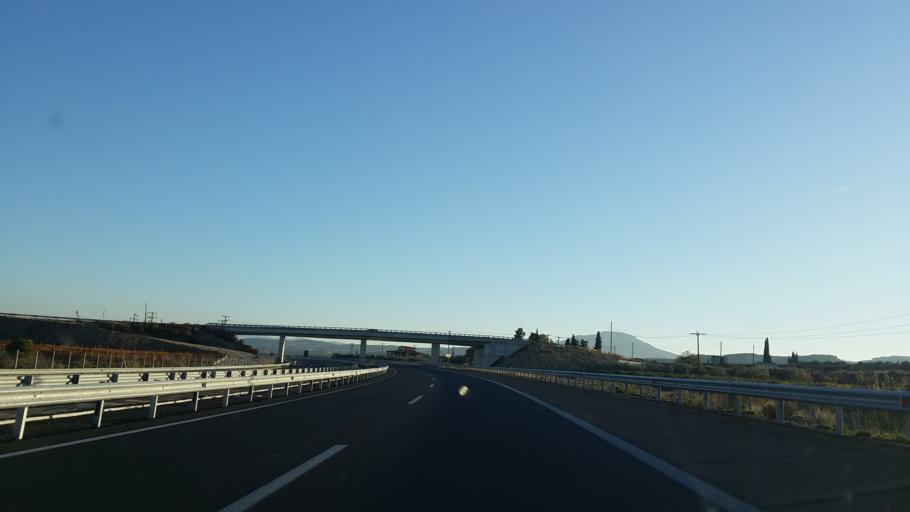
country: GR
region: Peloponnese
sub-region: Nomos Korinthias
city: Velo
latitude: 37.9619
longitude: 22.7484
